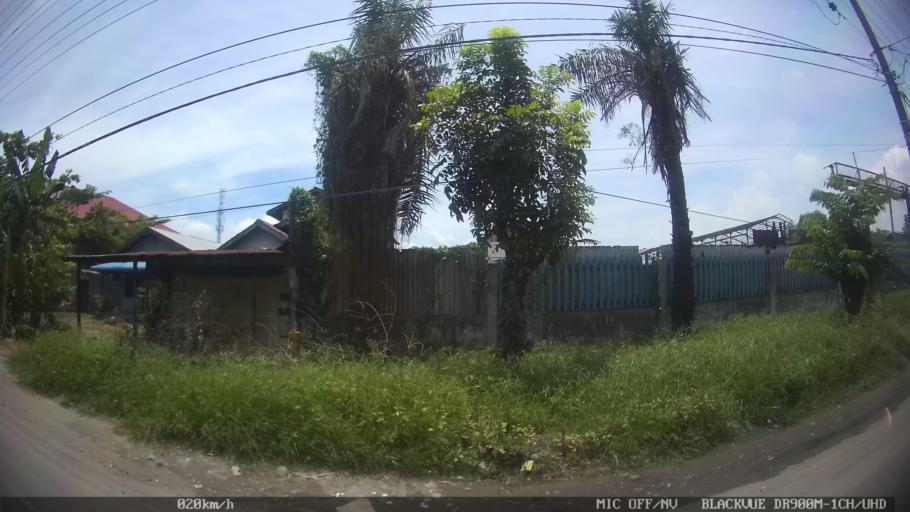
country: ID
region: North Sumatra
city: Belawan
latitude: 3.7567
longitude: 98.6773
